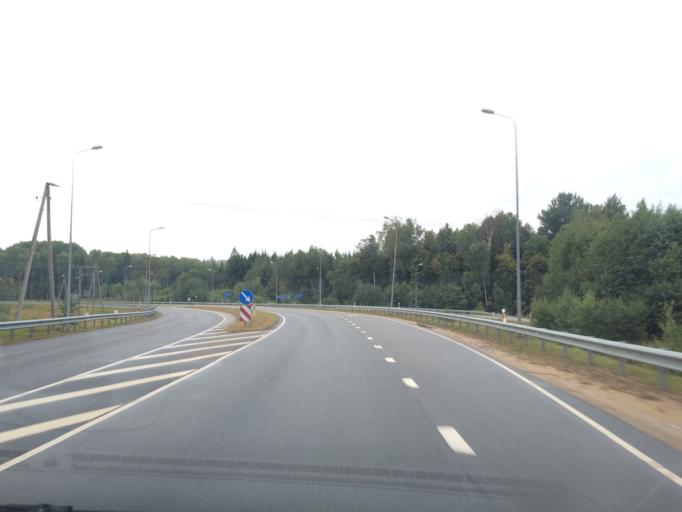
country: LV
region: Ogre
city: Ogre
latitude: 56.8579
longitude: 24.6446
